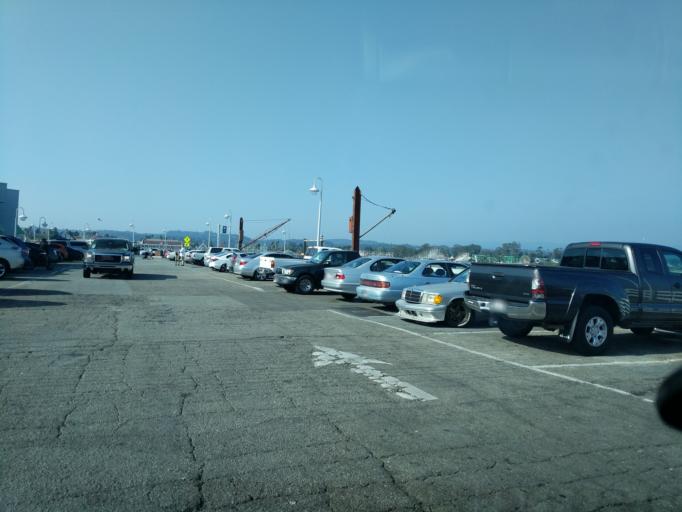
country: US
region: California
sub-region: Santa Cruz County
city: Santa Cruz
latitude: 36.9580
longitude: -122.0175
